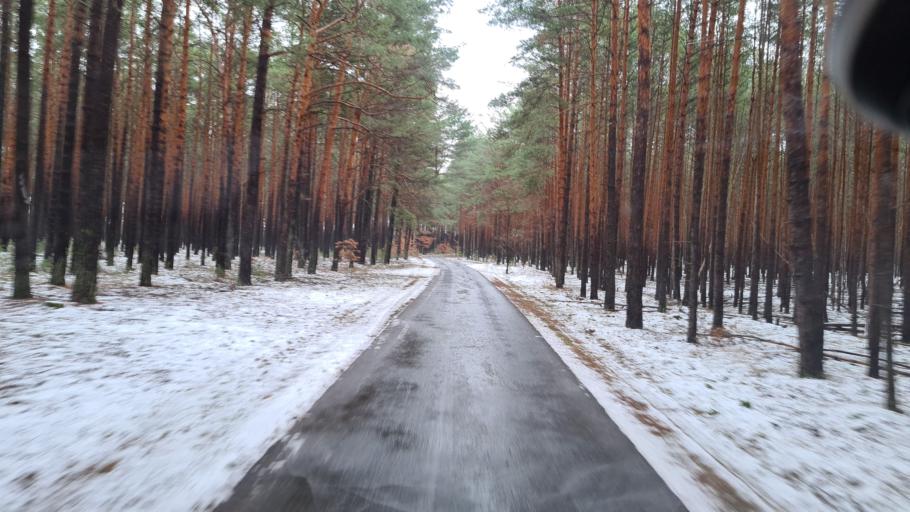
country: DE
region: Brandenburg
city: Janschwalde
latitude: 51.9008
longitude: 14.5302
